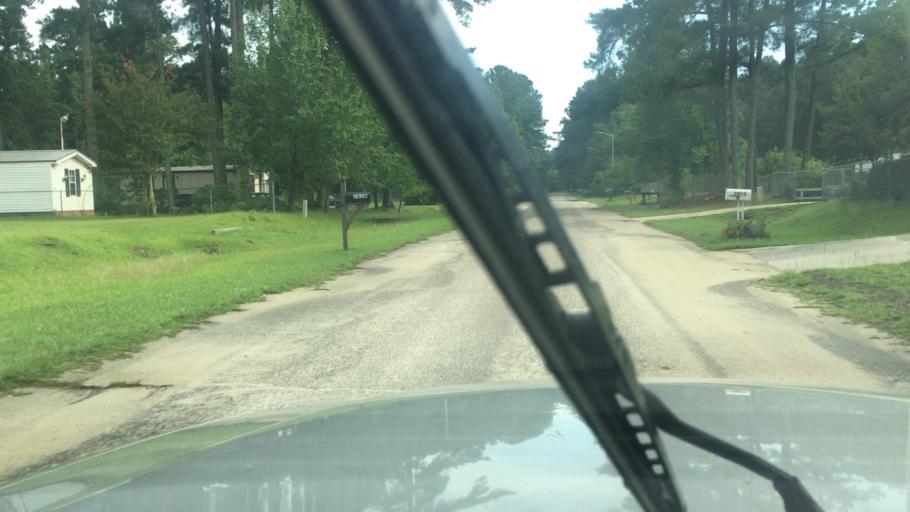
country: US
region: North Carolina
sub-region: Cumberland County
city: Eastover
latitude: 35.1532
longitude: -78.8638
